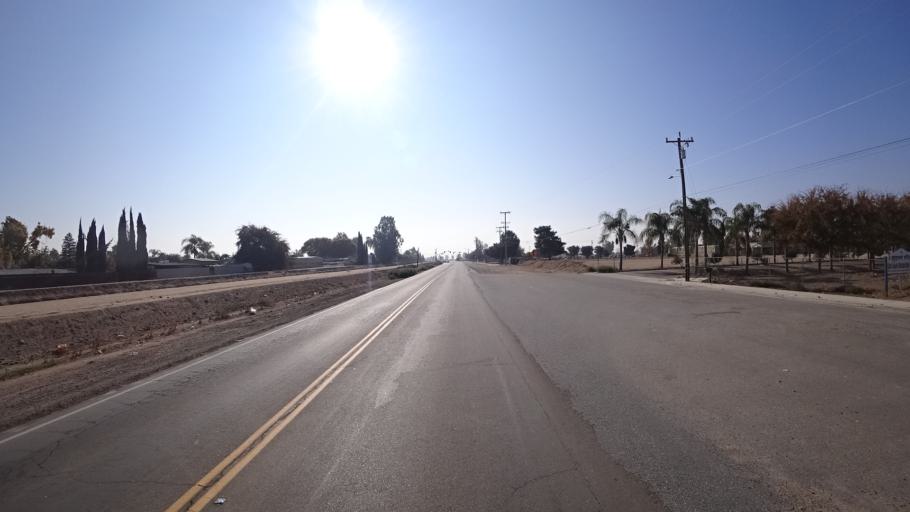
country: US
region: California
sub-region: Kern County
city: Greenfield
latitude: 35.2763
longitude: -119.0213
